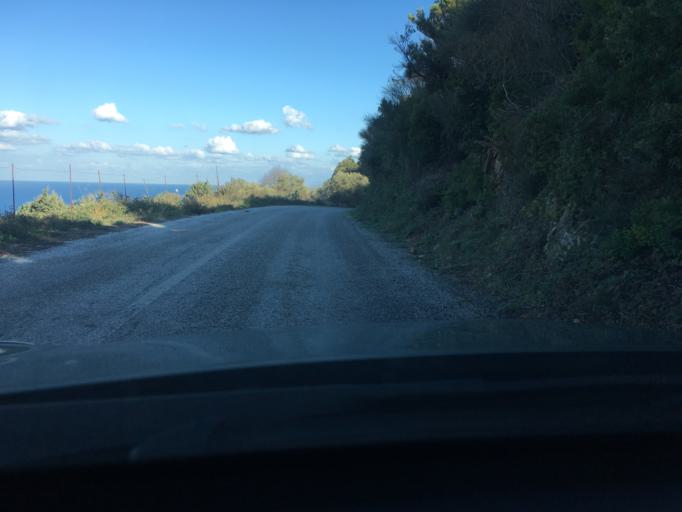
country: GR
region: Thessaly
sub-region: Nomos Magnisias
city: Skopelos
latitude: 39.1759
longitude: 23.6387
